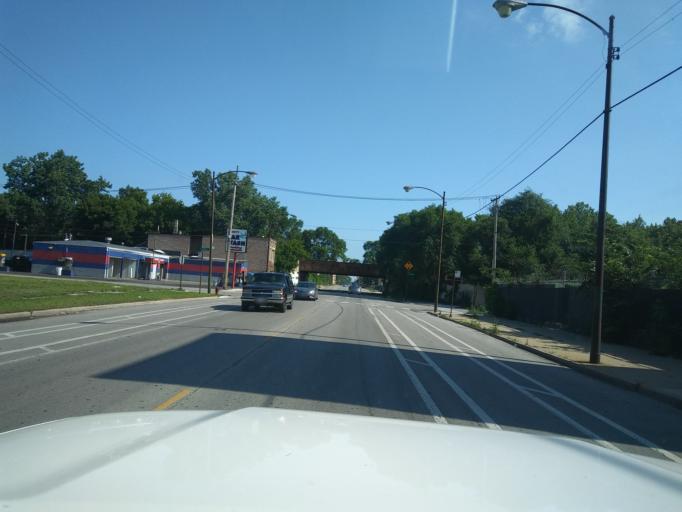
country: US
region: Illinois
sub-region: Cook County
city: Chicago
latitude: 41.8045
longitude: -87.6454
